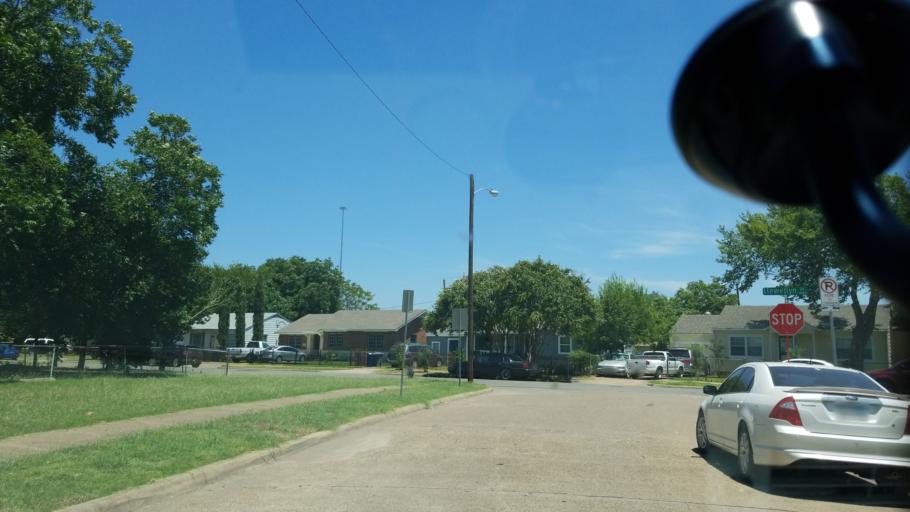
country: US
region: Texas
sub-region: Dallas County
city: Cockrell Hill
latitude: 32.7112
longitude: -96.8315
